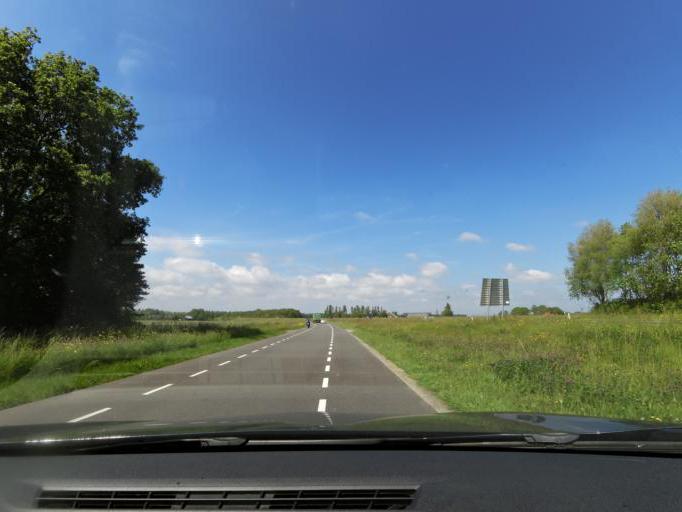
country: NL
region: South Holland
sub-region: Gemeente Hellevoetsluis
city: Nieuw-Helvoet
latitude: 51.8417
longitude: 4.0947
